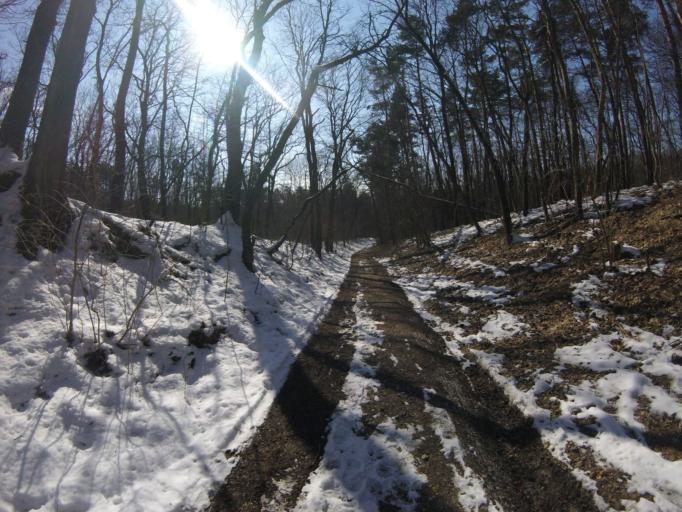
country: HU
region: Pest
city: Piliscsaba
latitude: 47.6400
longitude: 18.8560
